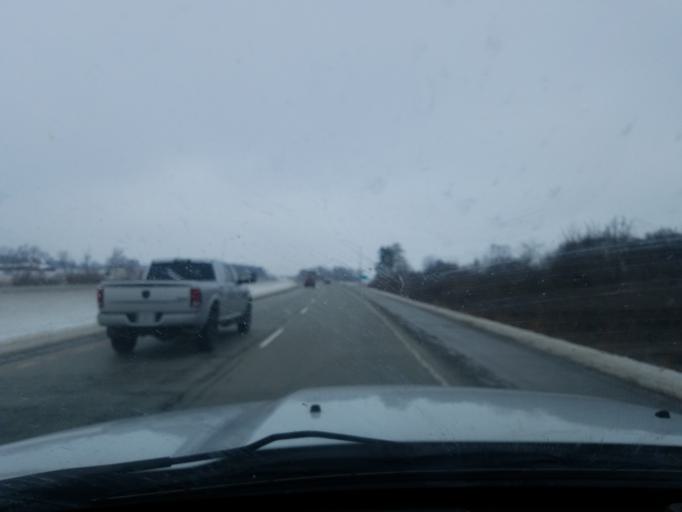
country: US
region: Indiana
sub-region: Marshall County
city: Argos
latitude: 41.1698
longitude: -86.2405
